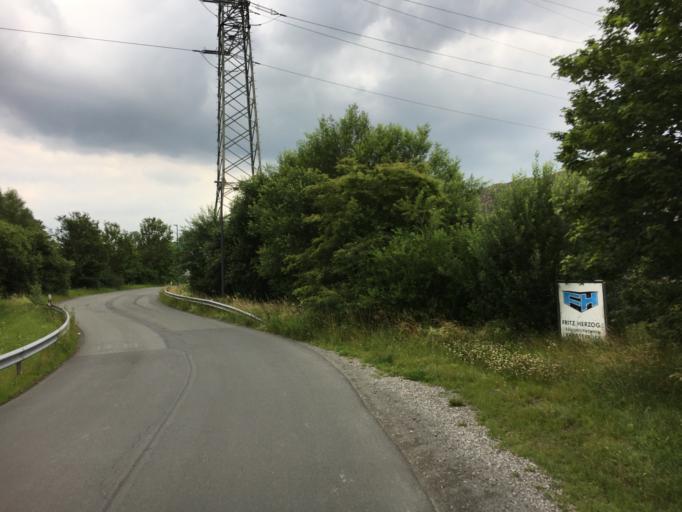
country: DE
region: North Rhine-Westphalia
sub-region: Regierungsbezirk Arnsberg
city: Erndtebruck
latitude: 50.9999
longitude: 8.2638
